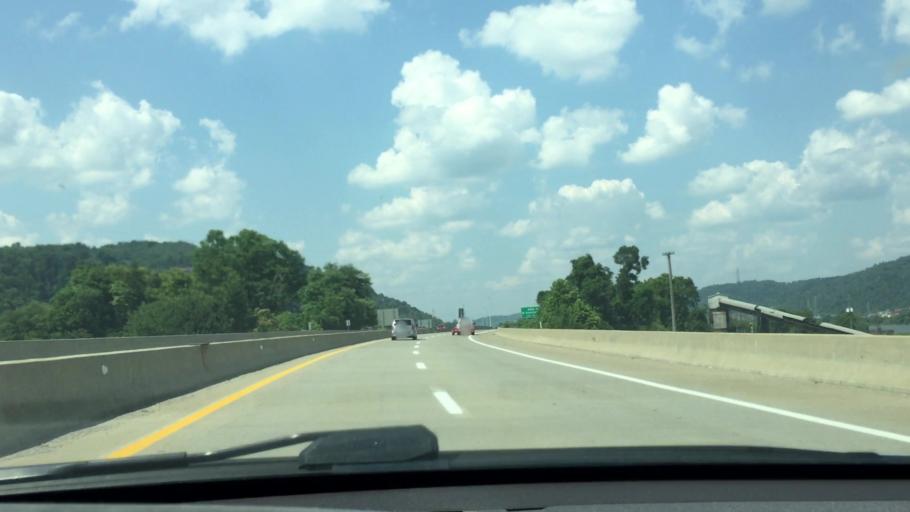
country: US
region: Ohio
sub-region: Belmont County
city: Bellaire
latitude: 40.0228
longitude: -80.7404
